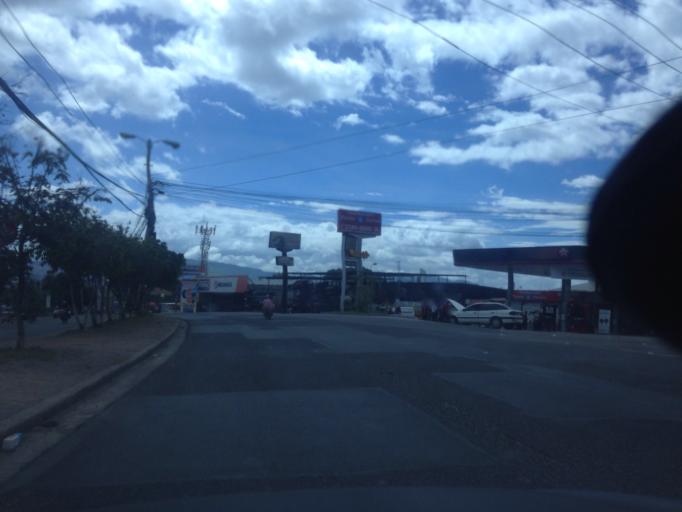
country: HN
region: Francisco Morazan
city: Tegucigalpa
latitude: 14.0749
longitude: -87.1810
